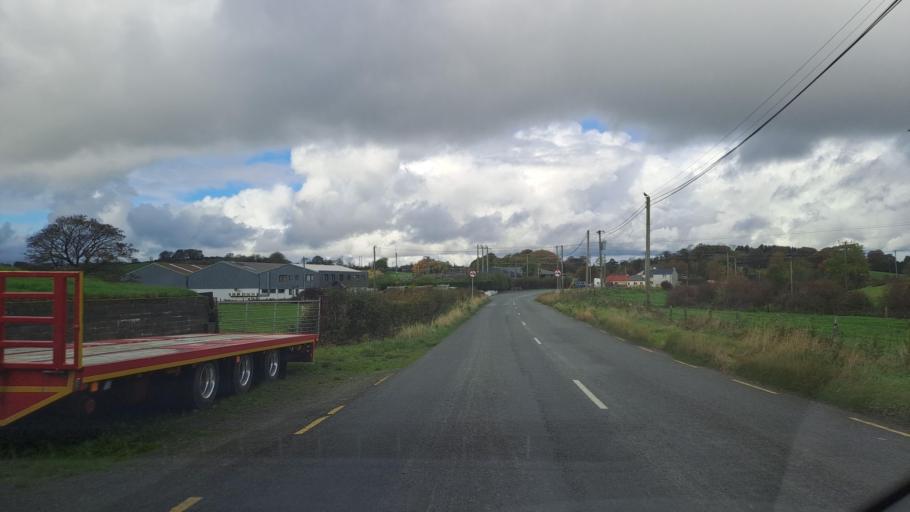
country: IE
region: Ulster
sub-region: An Cabhan
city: Bailieborough
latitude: 53.8944
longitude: -6.9662
